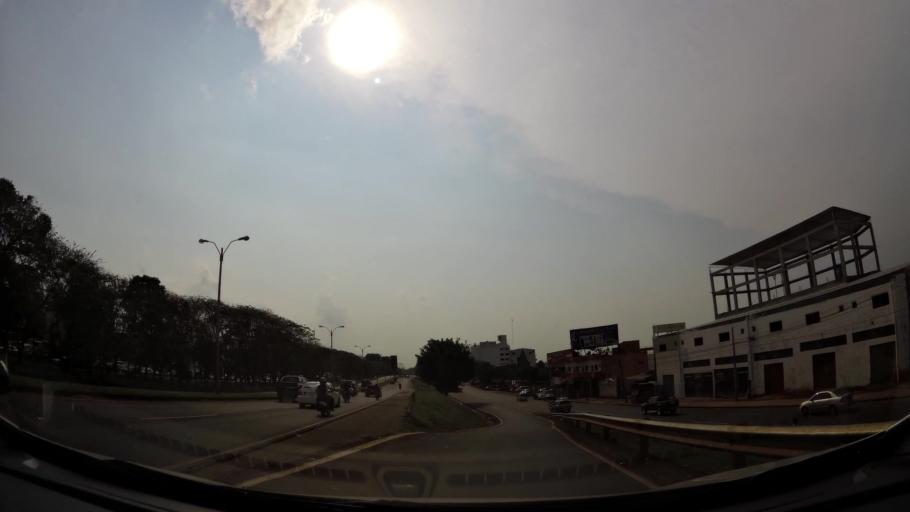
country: PY
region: Alto Parana
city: Ciudad del Este
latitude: -25.5060
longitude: -54.6417
